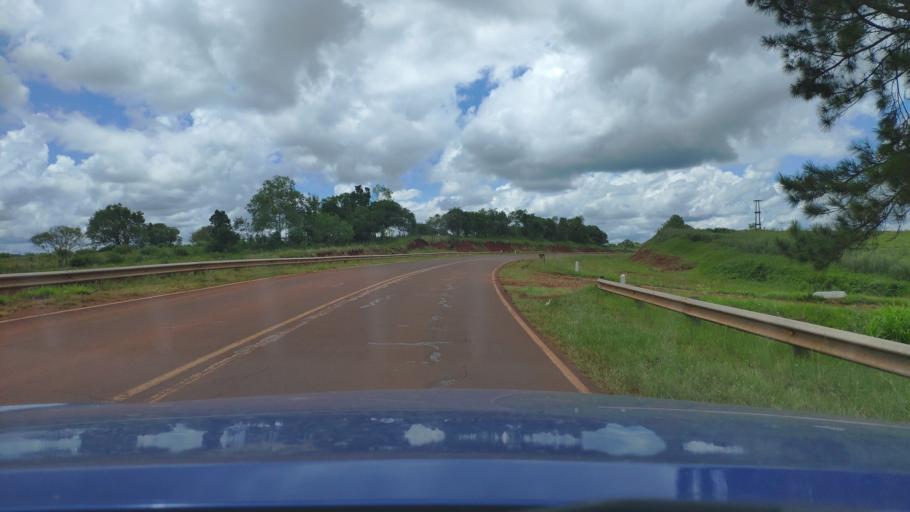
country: AR
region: Misiones
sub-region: Departamento de San Javier
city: San Javier
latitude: -27.8438
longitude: -55.2412
